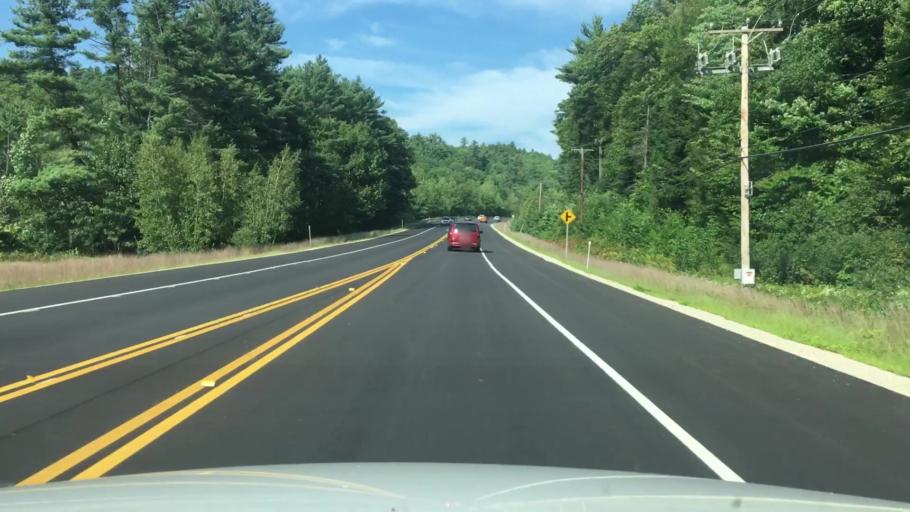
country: US
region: New Hampshire
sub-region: Belknap County
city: Gilford
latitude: 43.5366
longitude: -71.4331
